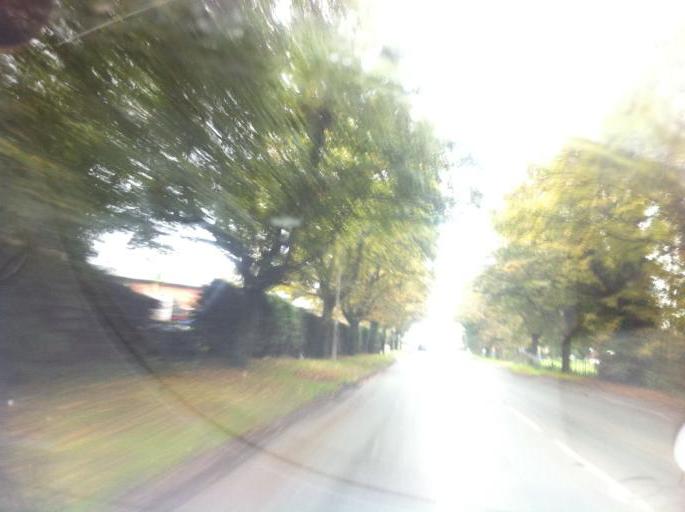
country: GB
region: England
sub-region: Lincolnshire
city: Wainfleet All Saints
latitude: 53.0376
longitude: 0.1197
